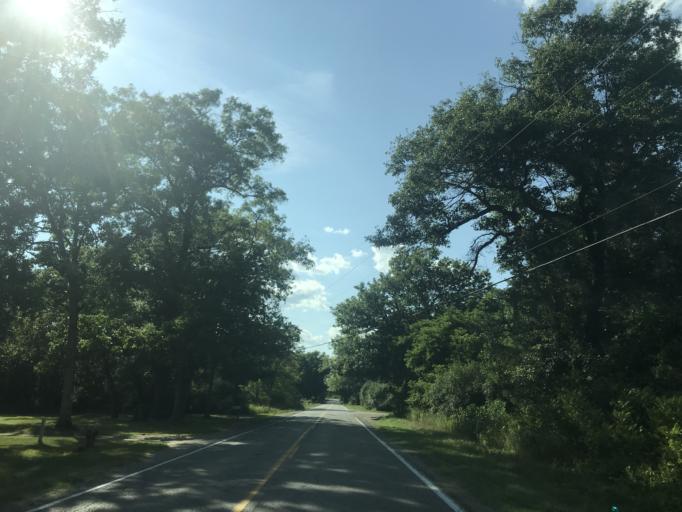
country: US
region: Michigan
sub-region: Newaygo County
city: Newaygo
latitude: 43.4256
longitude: -85.7713
